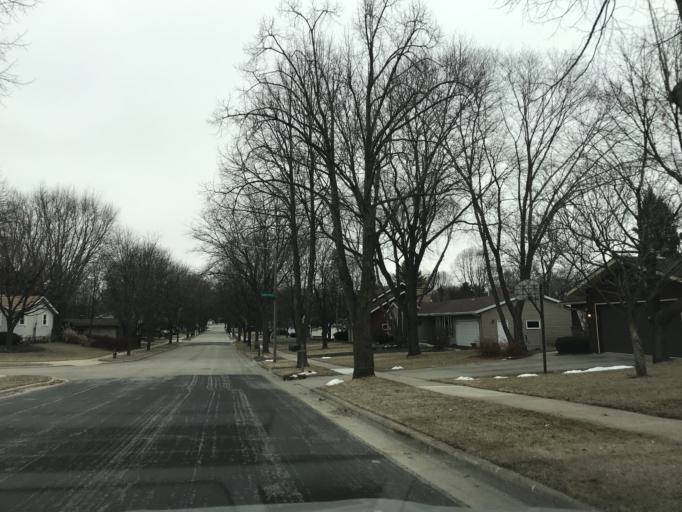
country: US
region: Wisconsin
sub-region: Dane County
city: Monona
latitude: 43.0921
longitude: -89.2928
